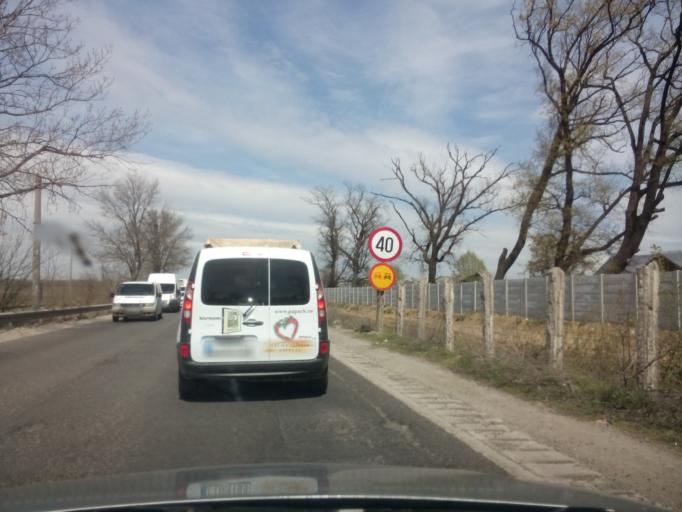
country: RO
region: Ilfov
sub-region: Comuna Pantelimon
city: Pantelimon
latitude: 44.4616
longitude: 26.2354
